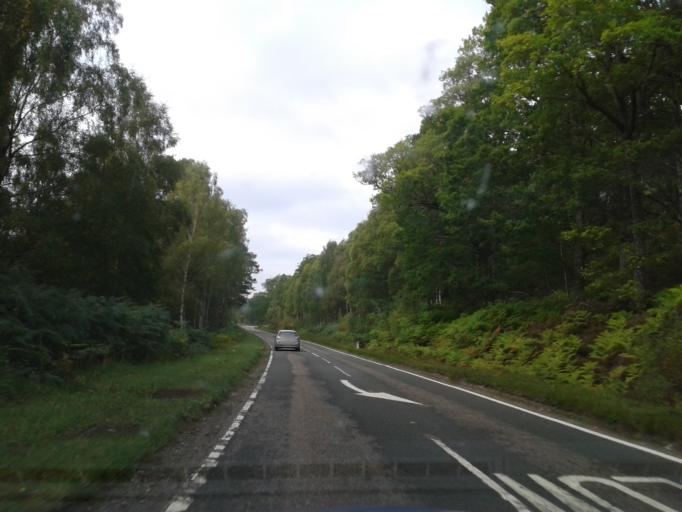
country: GB
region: Scotland
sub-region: Highland
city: Spean Bridge
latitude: 57.0810
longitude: -4.8724
